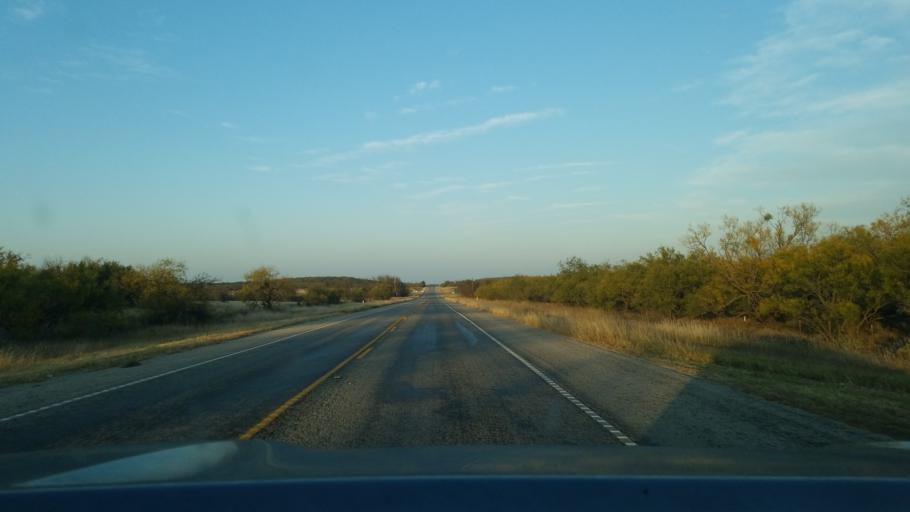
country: US
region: Texas
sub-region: Eastland County
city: Cisco
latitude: 32.4323
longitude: -98.9252
